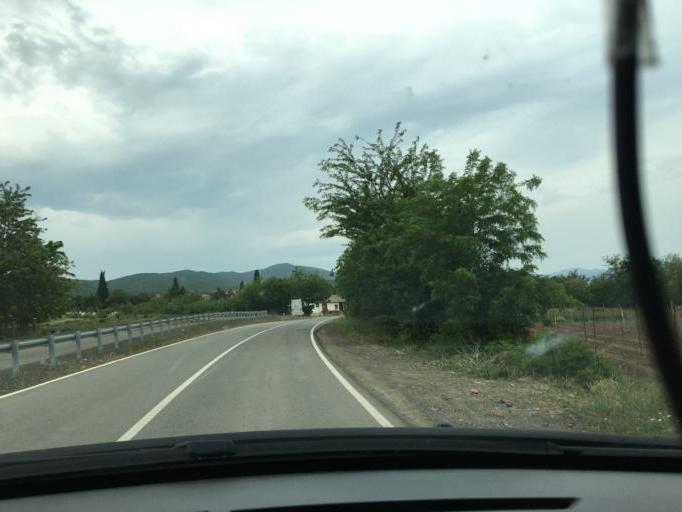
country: MK
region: Gevgelija
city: Miravci
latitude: 41.3044
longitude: 22.4429
